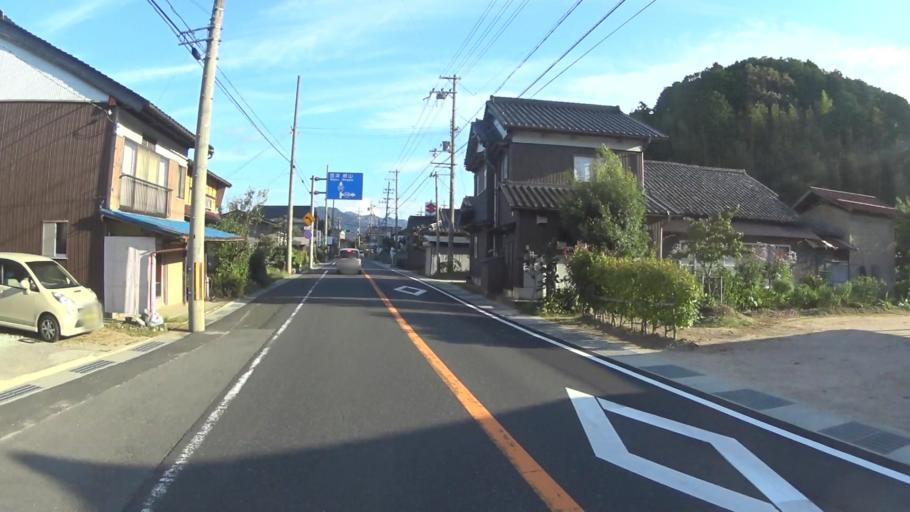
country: JP
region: Hyogo
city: Toyooka
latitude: 35.5900
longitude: 134.9242
